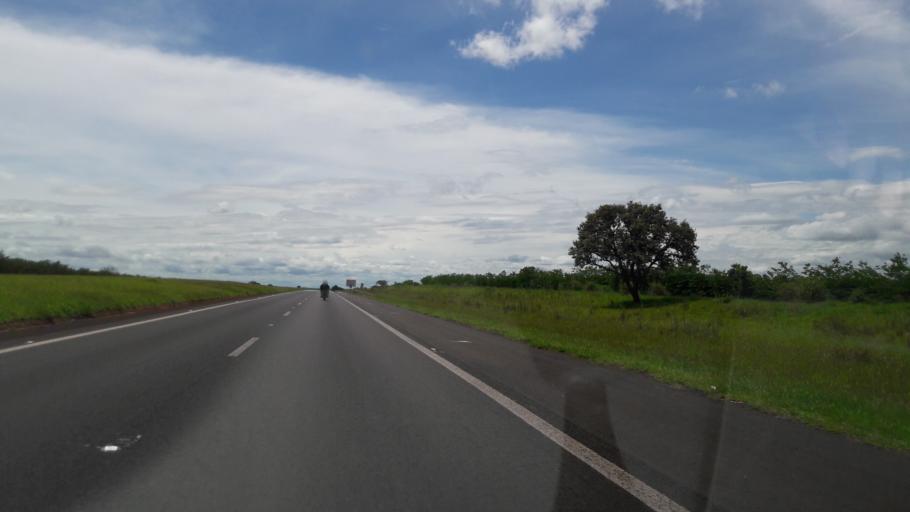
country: BR
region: Sao Paulo
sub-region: Avare
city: Avare
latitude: -22.9453
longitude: -48.8953
